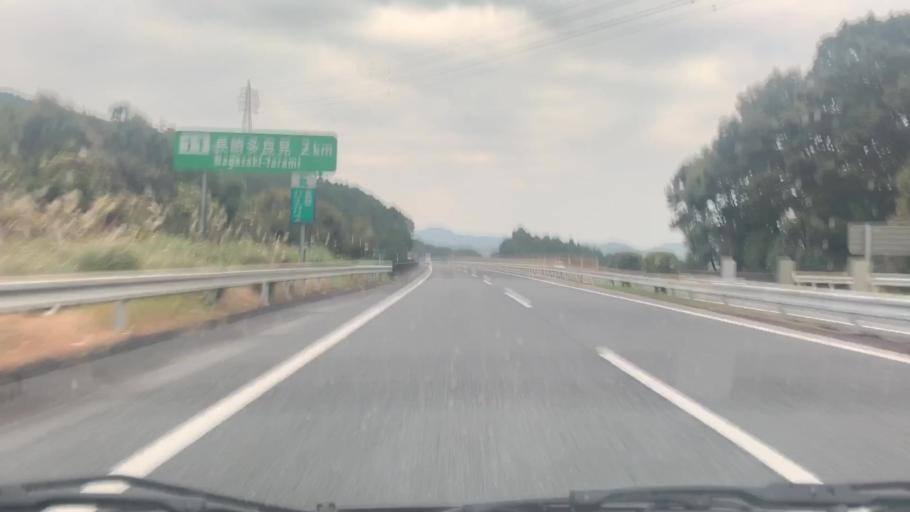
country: JP
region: Nagasaki
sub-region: Isahaya-shi
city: Isahaya
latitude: 32.8221
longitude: 129.9916
